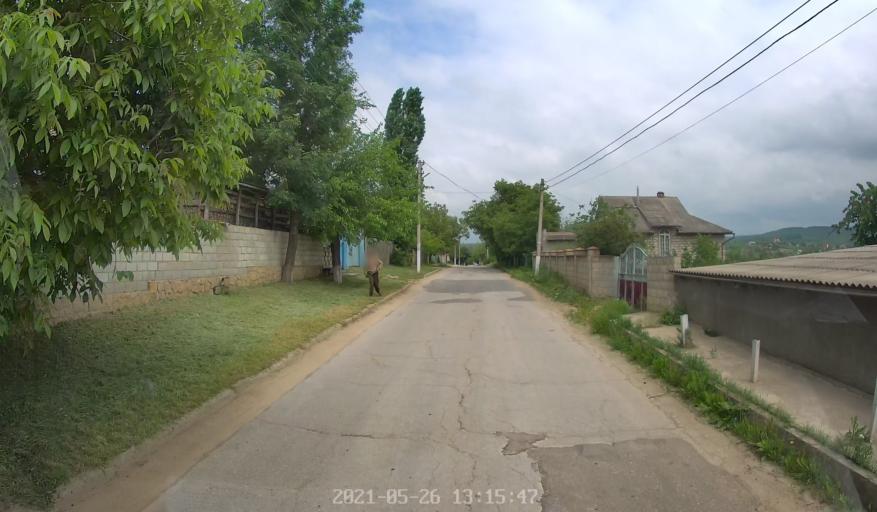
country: MD
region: Hincesti
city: Dancu
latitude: 46.7614
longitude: 28.3426
